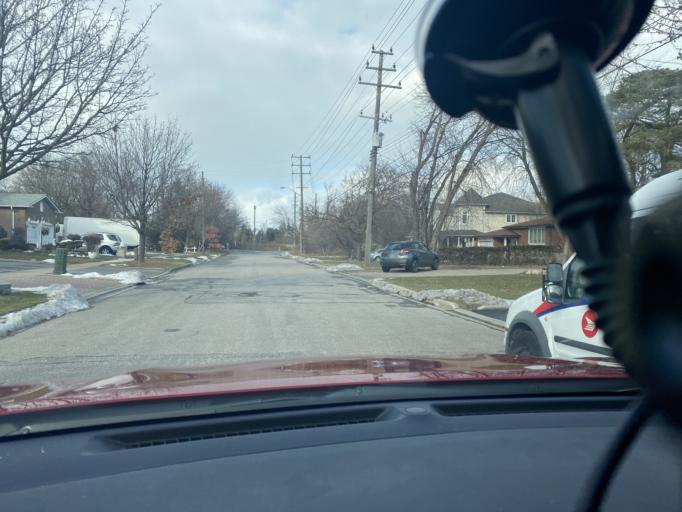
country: CA
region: Ontario
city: Scarborough
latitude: 43.7976
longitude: -79.1766
